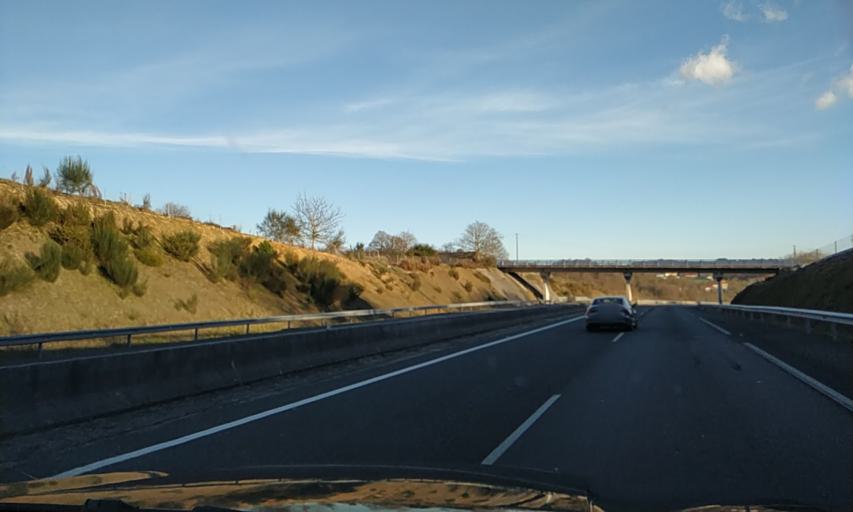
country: ES
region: Galicia
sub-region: Provincia de Pontevedra
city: Lalin
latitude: 42.6497
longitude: -8.1361
